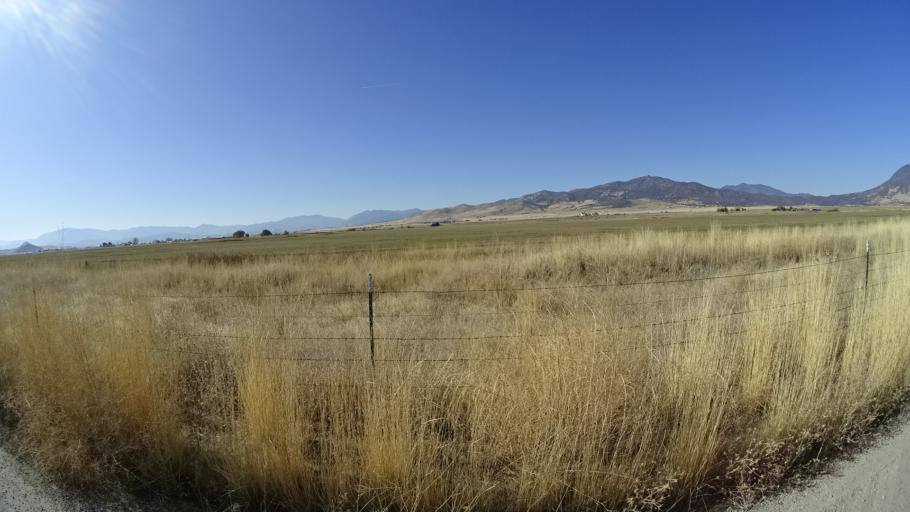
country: US
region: California
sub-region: Siskiyou County
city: Montague
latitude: 41.7873
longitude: -122.4613
